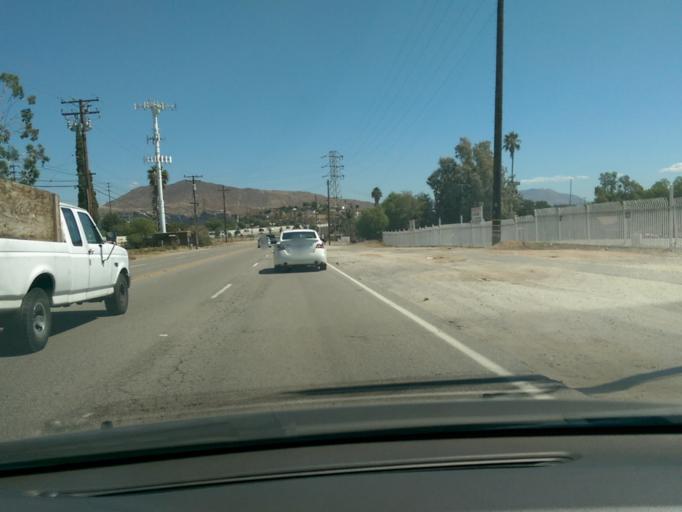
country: US
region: California
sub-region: Riverside County
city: Sunnyslope
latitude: 34.0120
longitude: -117.4394
